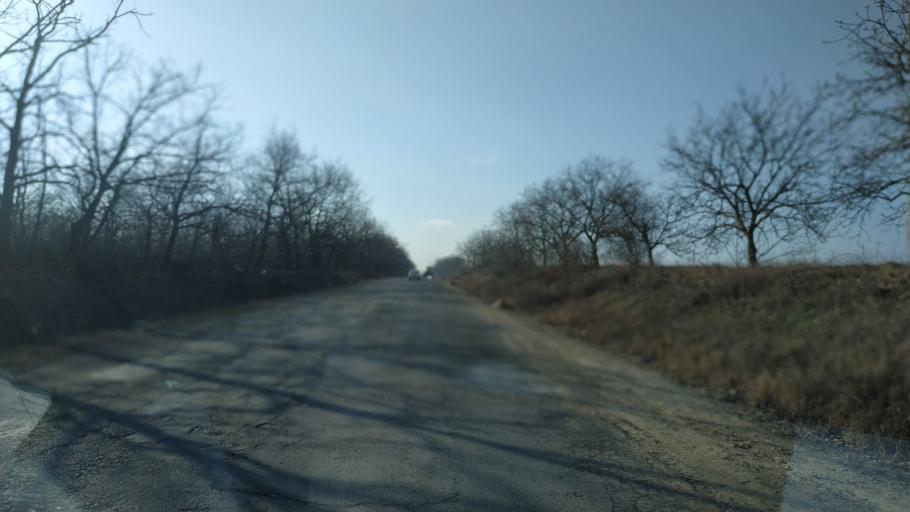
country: MD
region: Chisinau
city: Singera
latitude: 46.8724
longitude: 29.0397
